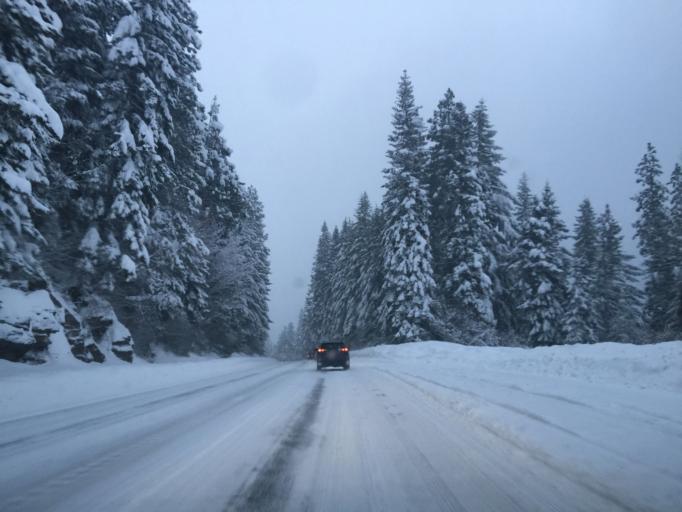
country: US
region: Washington
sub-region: Chelan County
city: Leavenworth
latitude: 47.7812
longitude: -120.9193
